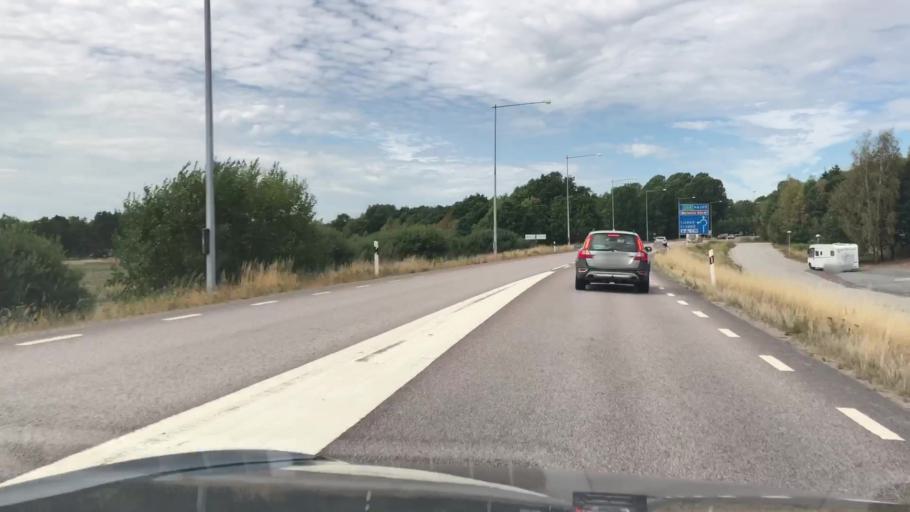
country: SE
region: Blekinge
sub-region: Karlskrona Kommun
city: Jaemjoe
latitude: 56.1831
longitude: 15.7251
